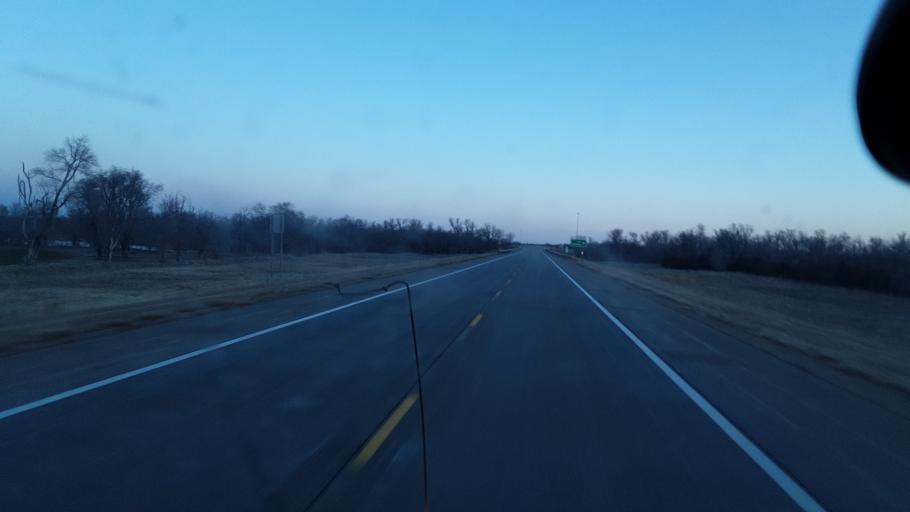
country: US
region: Kansas
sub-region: Reno County
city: South Hutchinson
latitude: 38.0484
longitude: -97.9858
